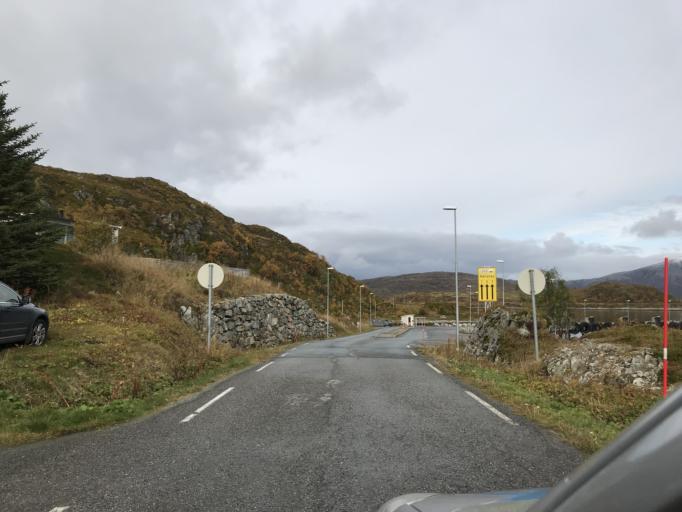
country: NO
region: Troms
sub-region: Tromso
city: Tromso
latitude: 70.0761
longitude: 18.9823
